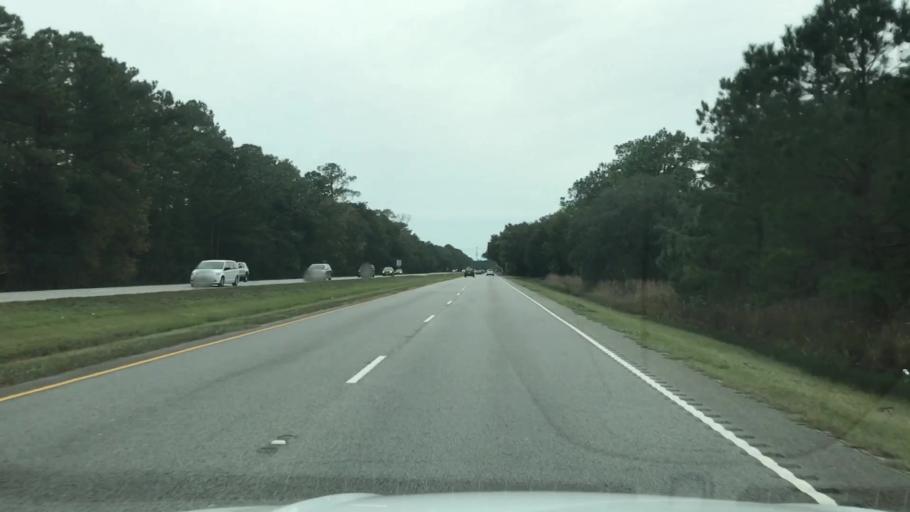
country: US
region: South Carolina
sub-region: Georgetown County
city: Georgetown
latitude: 33.3791
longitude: -79.2107
